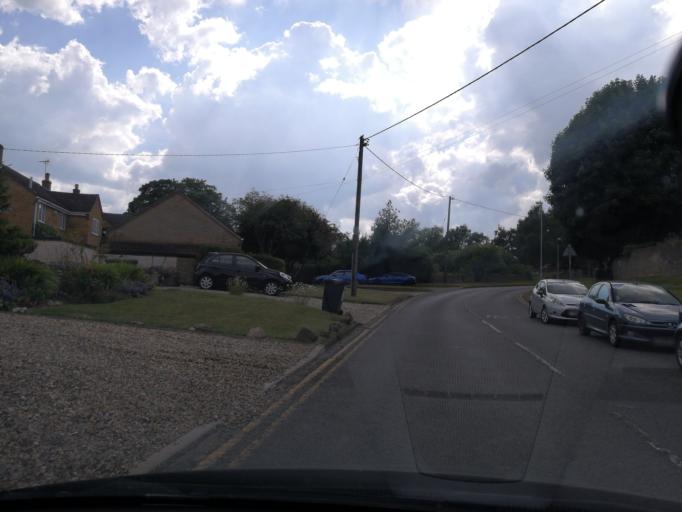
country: GB
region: England
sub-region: Cambridgeshire
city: Yaxley
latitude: 52.5116
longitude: -0.2648
